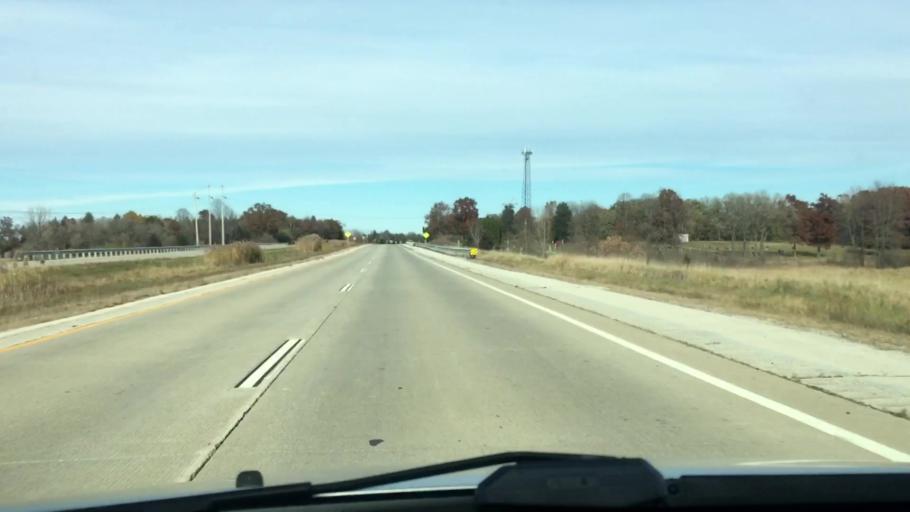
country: US
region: Wisconsin
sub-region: Brown County
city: Bellevue
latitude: 44.5914
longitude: -87.8646
